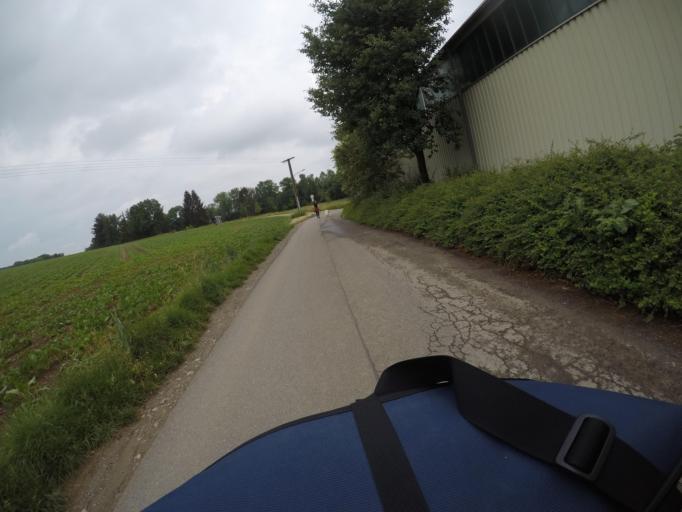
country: DE
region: Baden-Wuerttemberg
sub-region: Regierungsbezirk Stuttgart
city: Ditzingen
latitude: 48.8371
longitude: 9.0585
